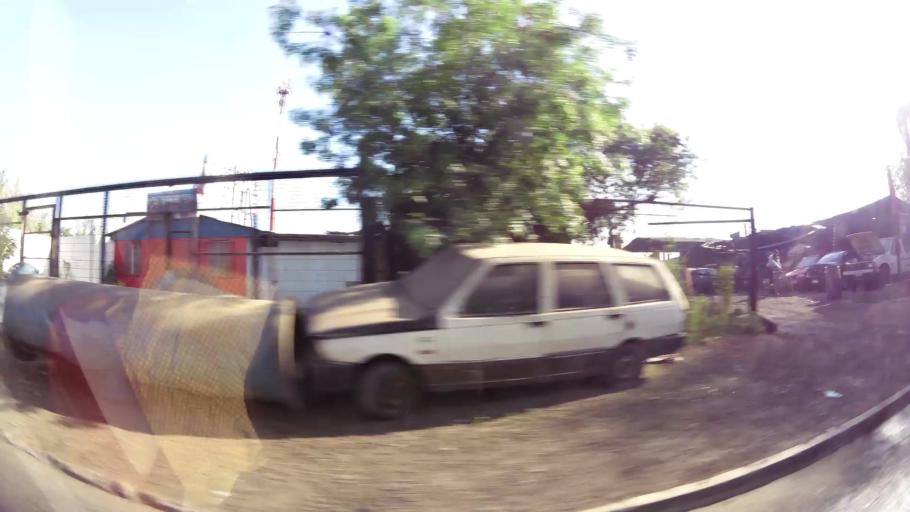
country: CL
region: Santiago Metropolitan
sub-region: Provincia de Santiago
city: Lo Prado
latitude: -33.4140
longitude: -70.7616
